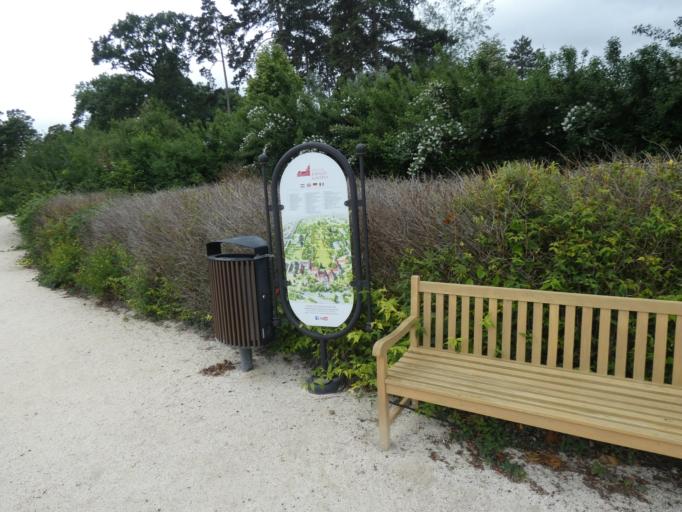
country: HU
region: Pest
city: Godollo
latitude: 47.5945
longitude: 19.3452
